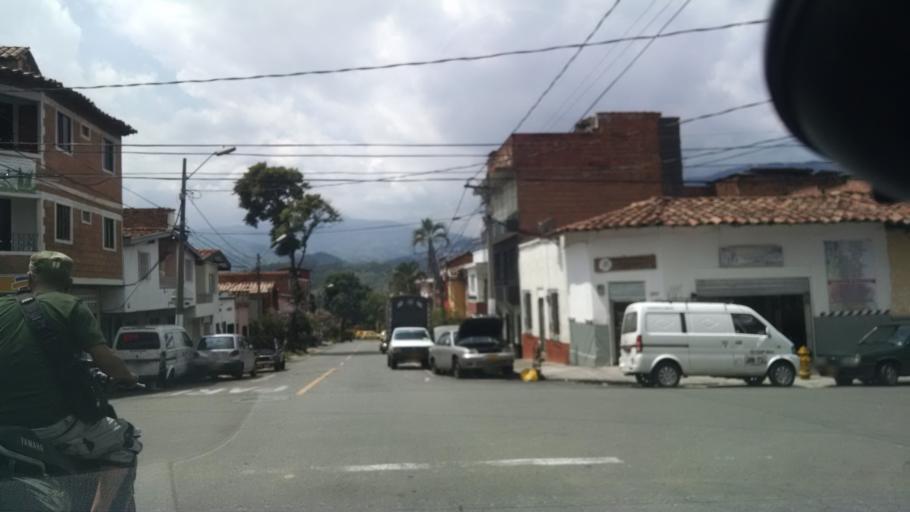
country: CO
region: Antioquia
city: Medellin
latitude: 6.2651
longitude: -75.5584
